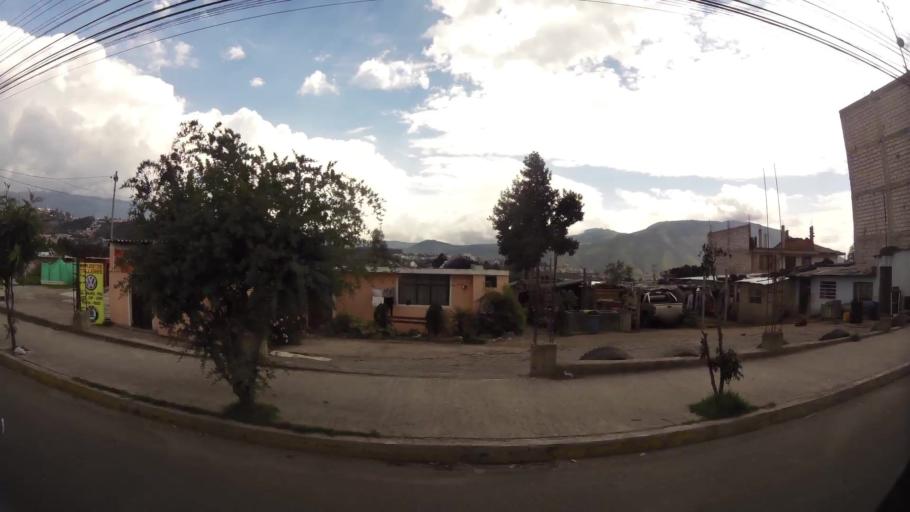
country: EC
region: Pichincha
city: Quito
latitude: -0.0955
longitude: -78.4438
